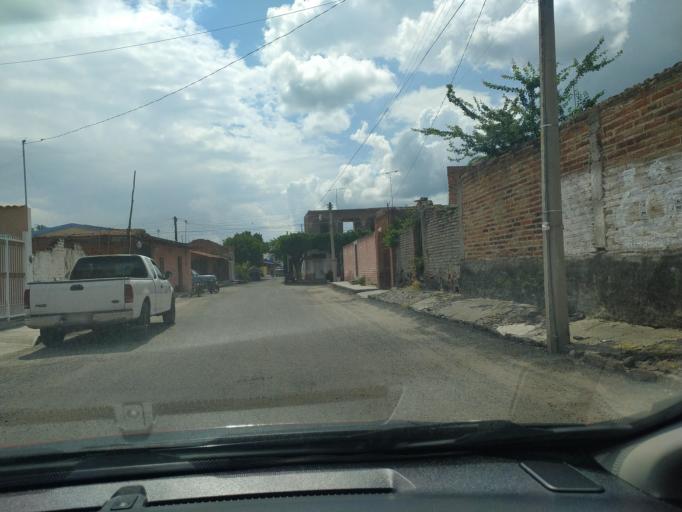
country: MX
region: Jalisco
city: Villa Corona
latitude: 20.3494
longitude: -103.6737
